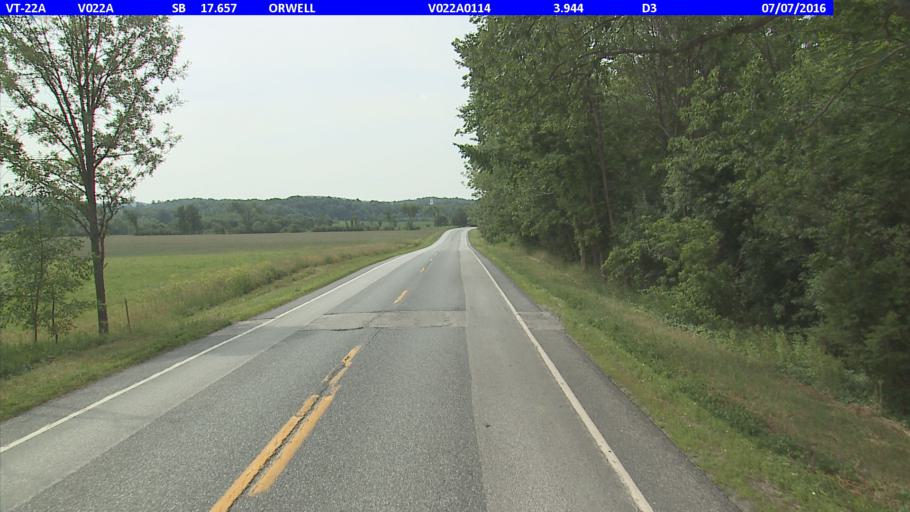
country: US
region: New York
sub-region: Essex County
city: Ticonderoga
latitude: 43.8137
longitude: -73.3050
